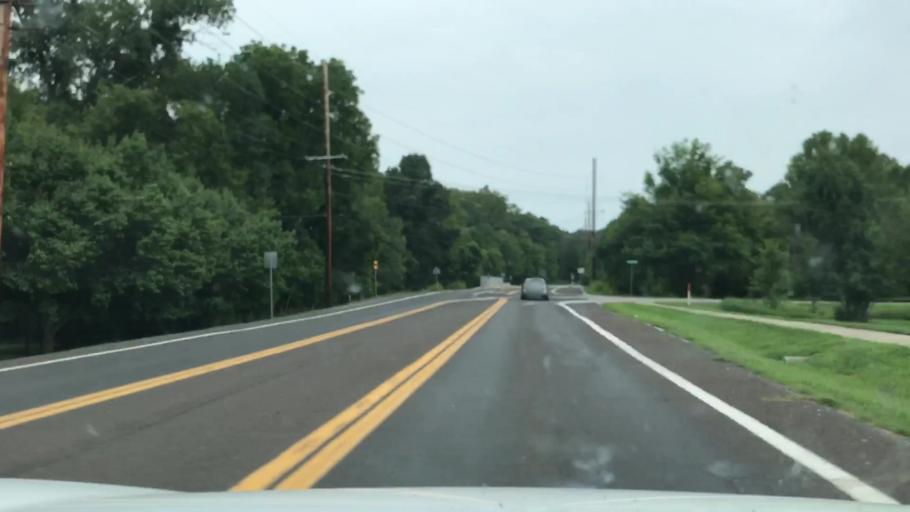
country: US
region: Missouri
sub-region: Saint Louis County
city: Clarkson Valley
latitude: 38.6435
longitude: -90.6124
